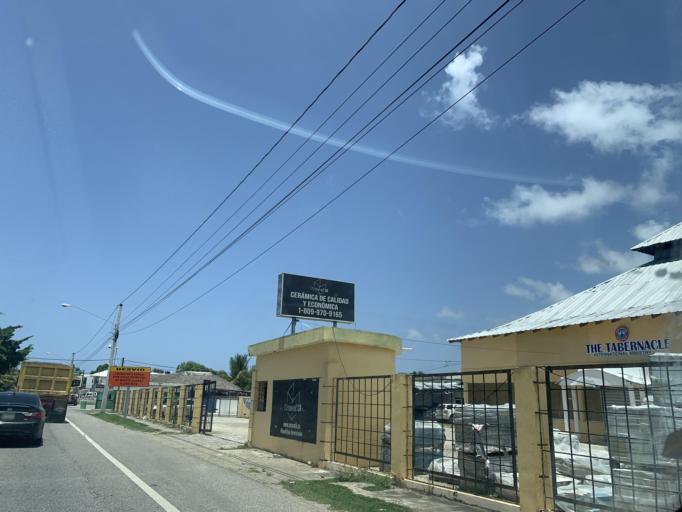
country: DO
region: Puerto Plata
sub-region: Puerto Plata
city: Puerto Plata
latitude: 19.7288
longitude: -70.6069
